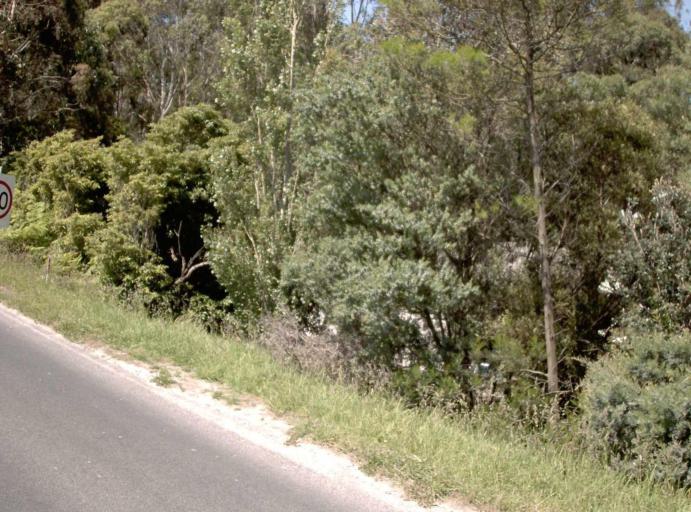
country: AU
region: Victoria
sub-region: Latrobe
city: Morwell
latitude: -38.6567
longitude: 146.1932
